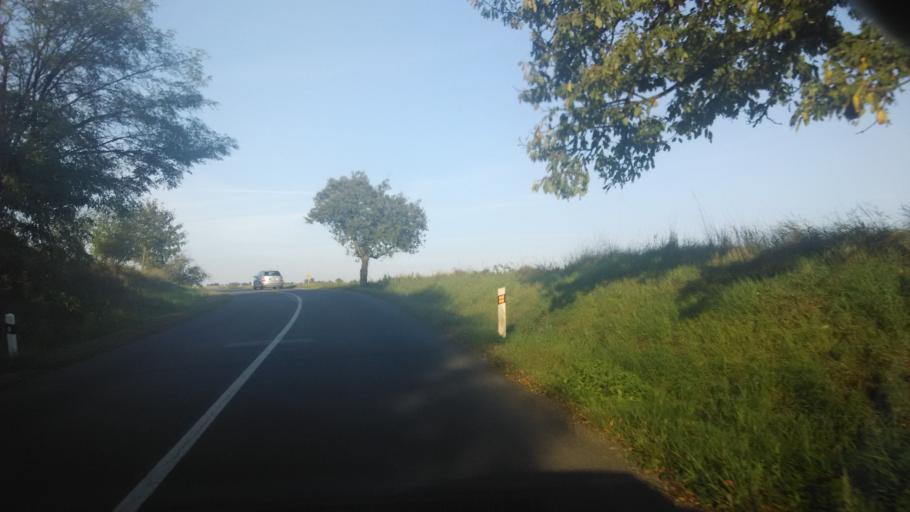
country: SK
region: Banskobystricky
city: Dudince
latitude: 48.2057
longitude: 18.7977
